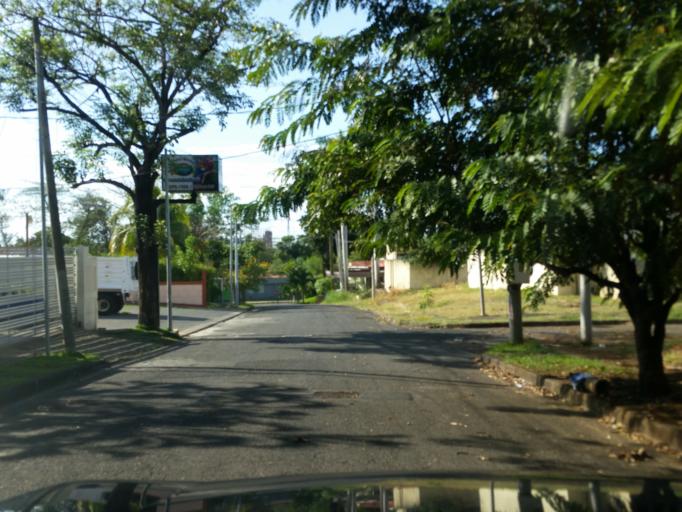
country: NI
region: Managua
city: Managua
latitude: 12.1198
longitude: -86.2644
